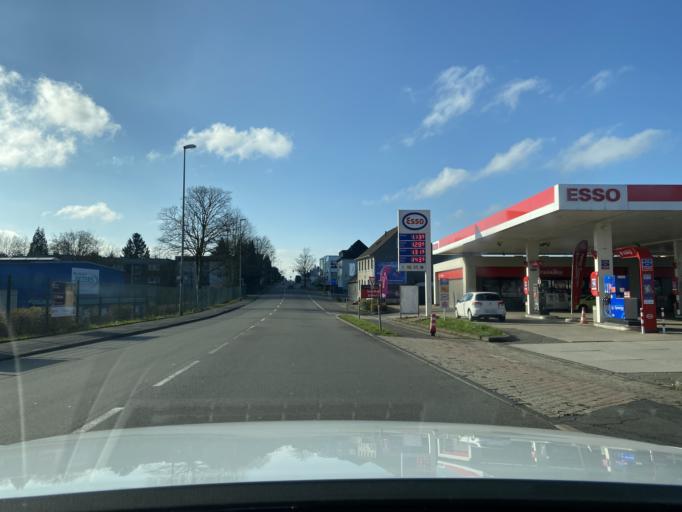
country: DE
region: North Rhine-Westphalia
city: Wermelskirchen
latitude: 51.1799
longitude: 7.2543
